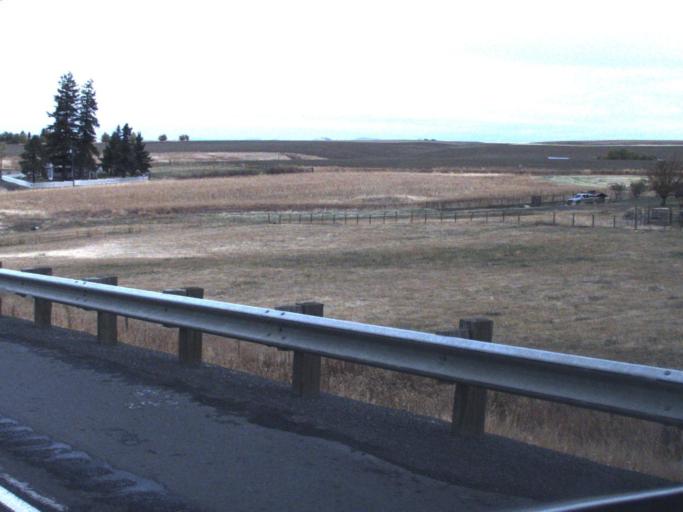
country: US
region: Washington
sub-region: Asotin County
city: Clarkston
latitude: 46.5265
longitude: -117.0841
